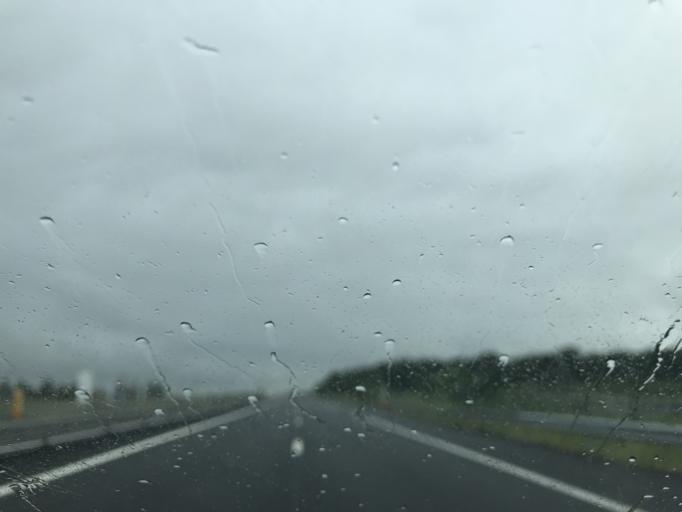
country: FR
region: Centre
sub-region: Departement du Cher
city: Marmagne
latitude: 47.0952
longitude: 2.2417
